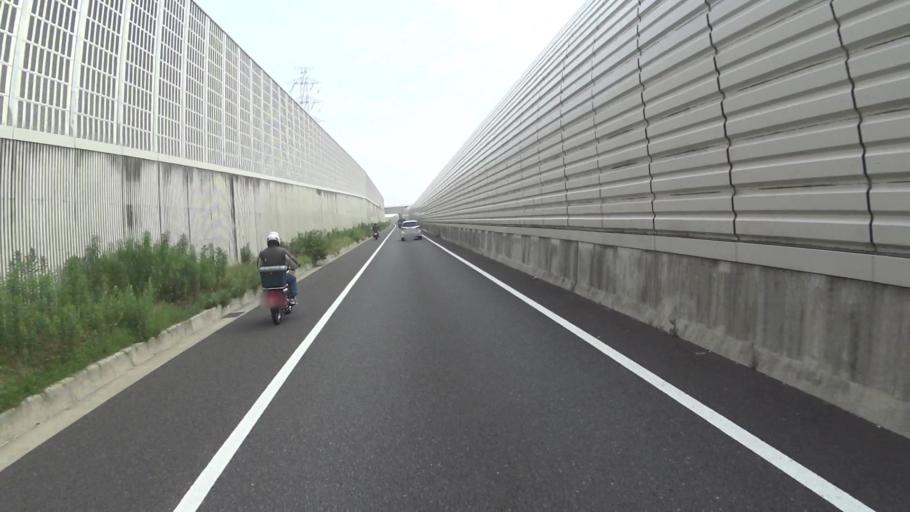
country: JP
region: Osaka
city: Hirakata
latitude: 34.8039
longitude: 135.7080
